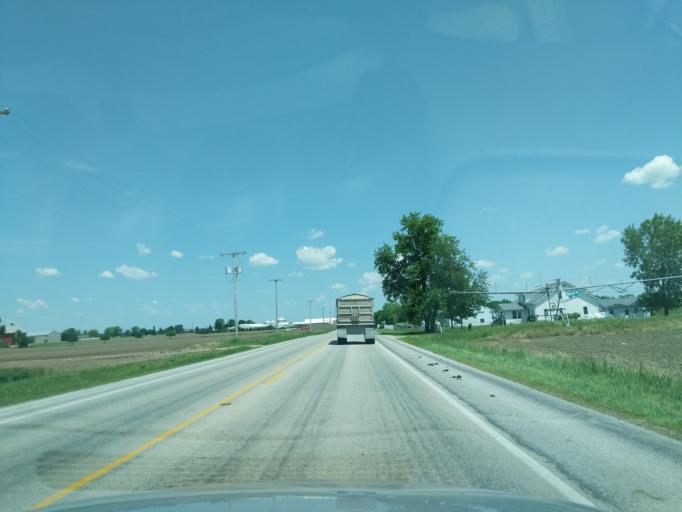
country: US
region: Indiana
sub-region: LaGrange County
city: Topeka
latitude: 41.5172
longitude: -85.5779
